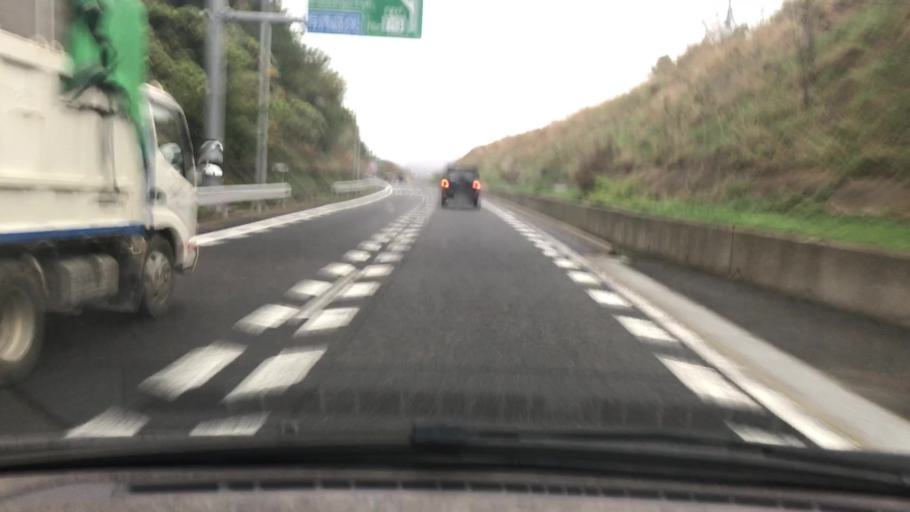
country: JP
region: Hyogo
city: Sandacho
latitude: 34.8111
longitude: 135.2471
